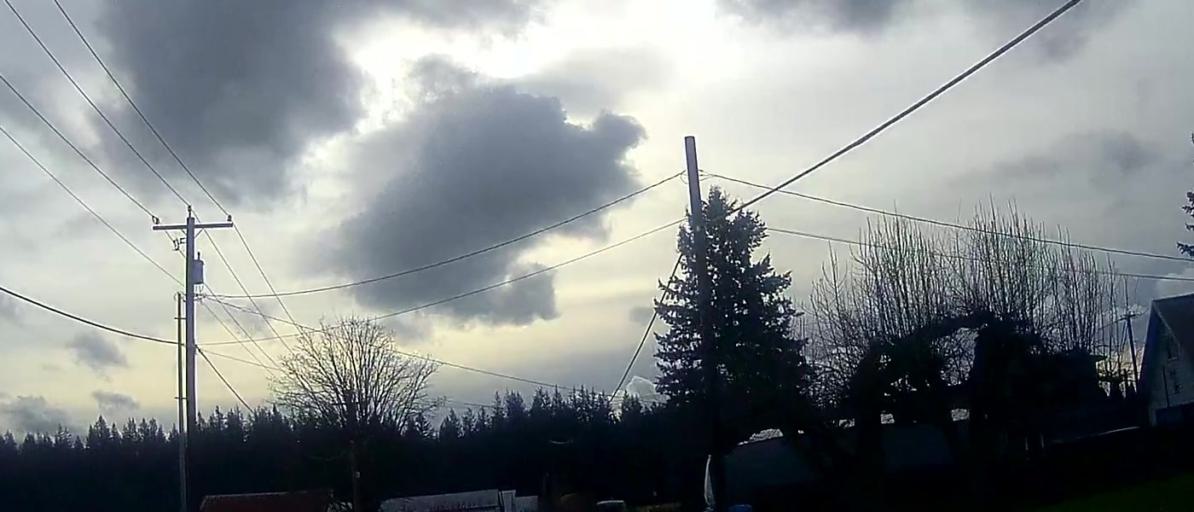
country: US
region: Washington
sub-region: Skagit County
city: Burlington
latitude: 48.5594
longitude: -122.3274
